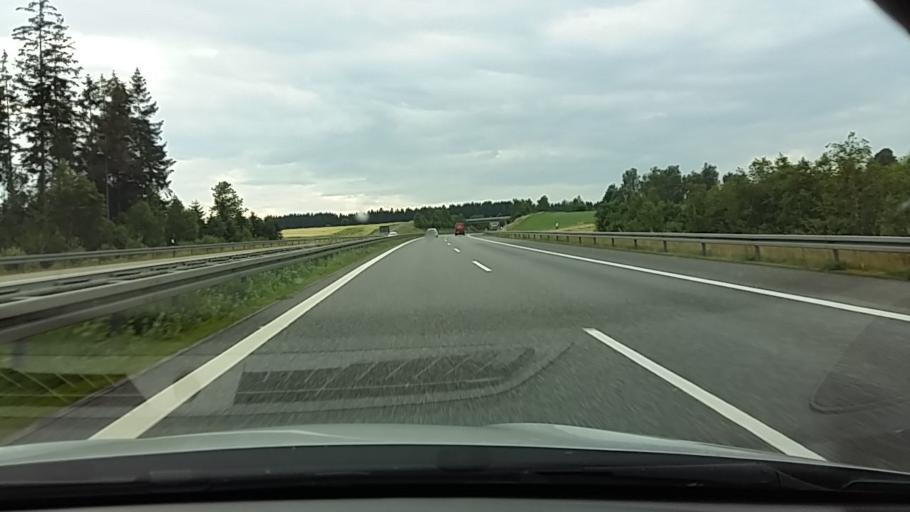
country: DE
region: Bavaria
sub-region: Upper Palatinate
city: Moosbach
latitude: 49.6117
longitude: 12.3860
